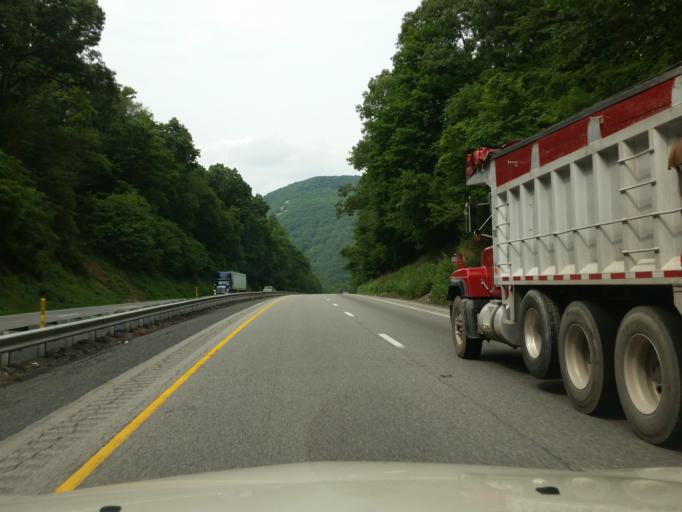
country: US
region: Pennsylvania
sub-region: Mifflin County
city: Yeagertown
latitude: 40.6422
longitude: -77.5846
